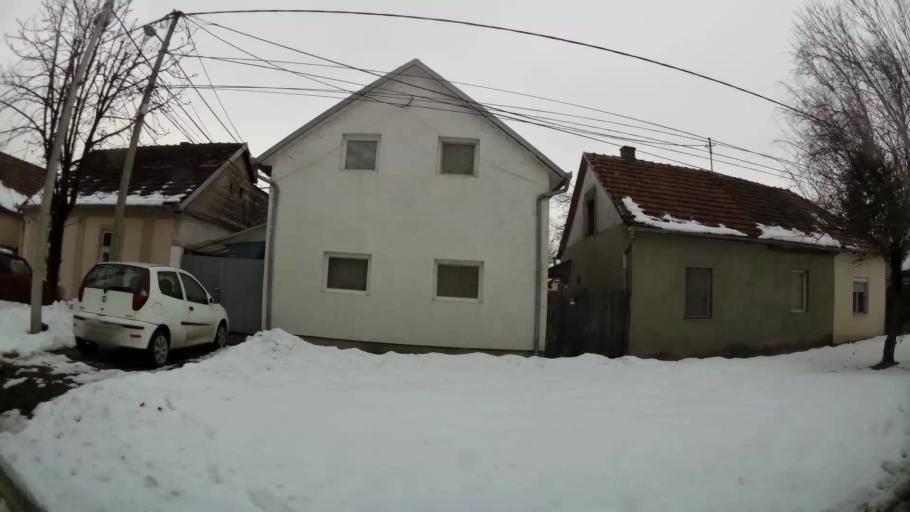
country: RS
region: Central Serbia
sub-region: Belgrade
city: Zemun
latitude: 44.8547
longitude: 20.3802
